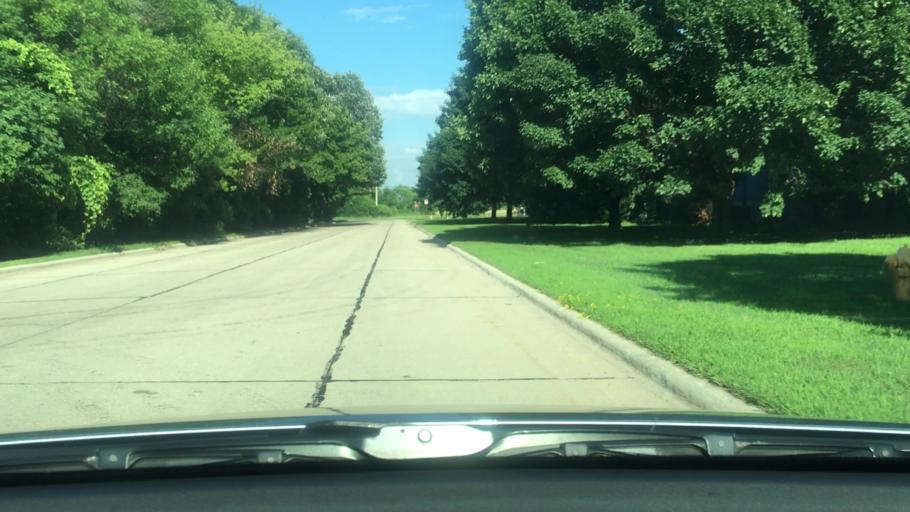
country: US
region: Wisconsin
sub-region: Winnebago County
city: Oshkosh
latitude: 43.9734
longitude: -88.5450
